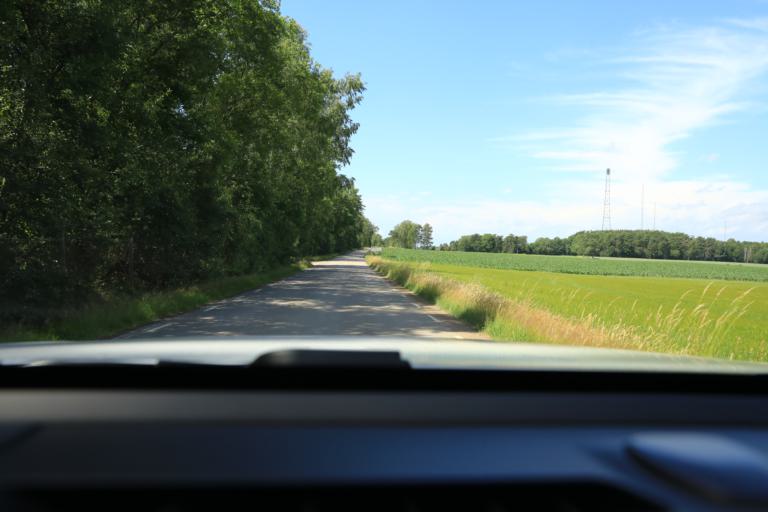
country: SE
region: Halland
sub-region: Varbergs Kommun
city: Tvaaker
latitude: 57.0959
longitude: 12.3910
